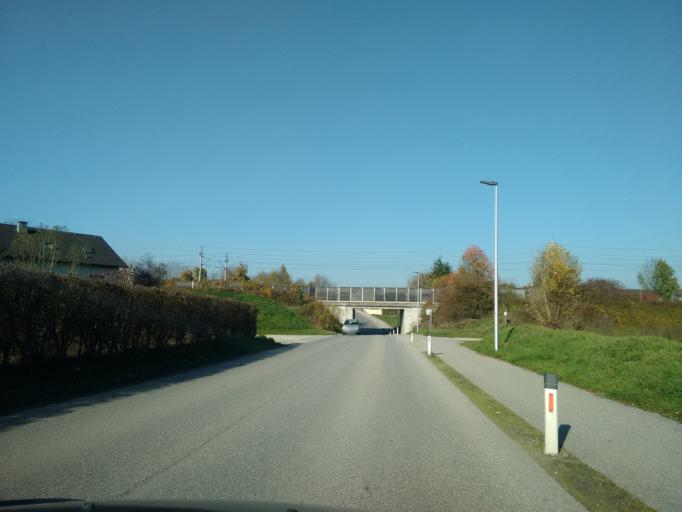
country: AT
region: Upper Austria
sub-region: Wels-Land
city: Gunskirchen
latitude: 48.1448
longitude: 13.9659
